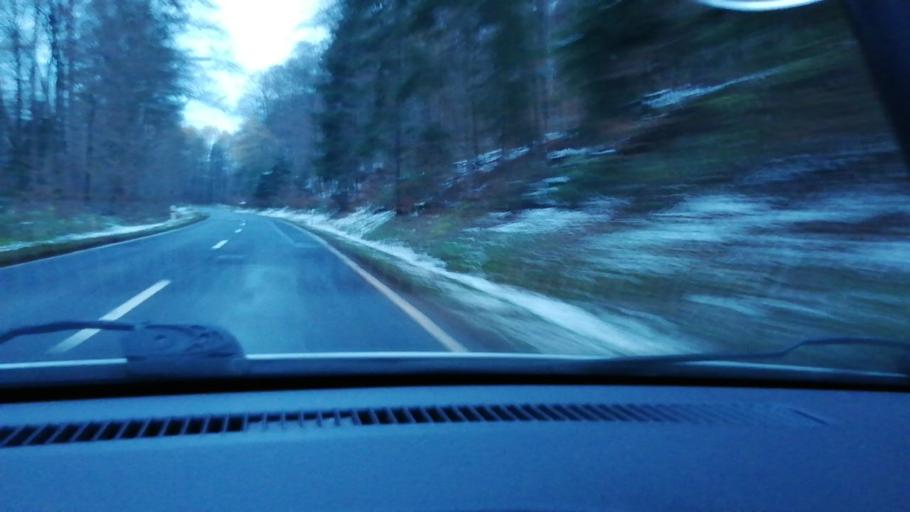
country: DE
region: Bavaria
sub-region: Regierungsbezirk Unterfranken
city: Geiselbach
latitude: 50.1369
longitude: 9.1772
